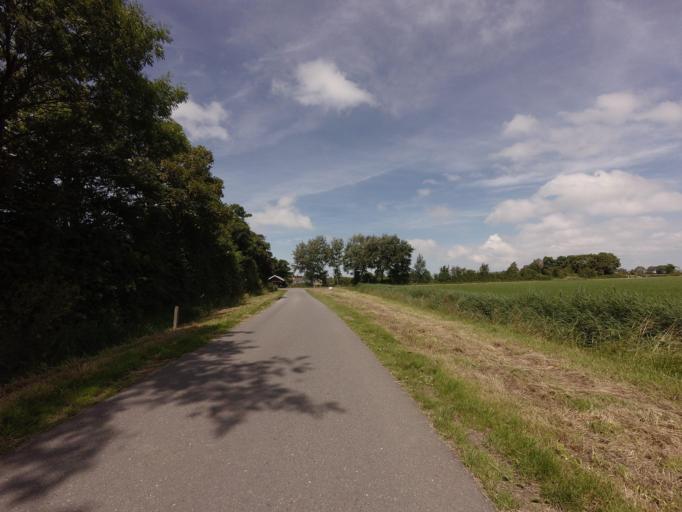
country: NL
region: North Holland
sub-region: Gemeente Texel
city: Den Burg
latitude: 53.0827
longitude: 4.8799
